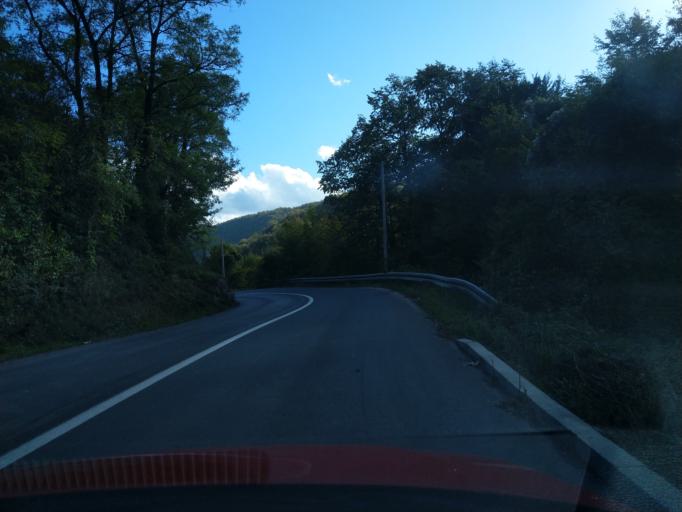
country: RS
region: Central Serbia
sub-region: Zlatiborski Okrug
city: Uzice
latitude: 43.8761
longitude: 19.7919
